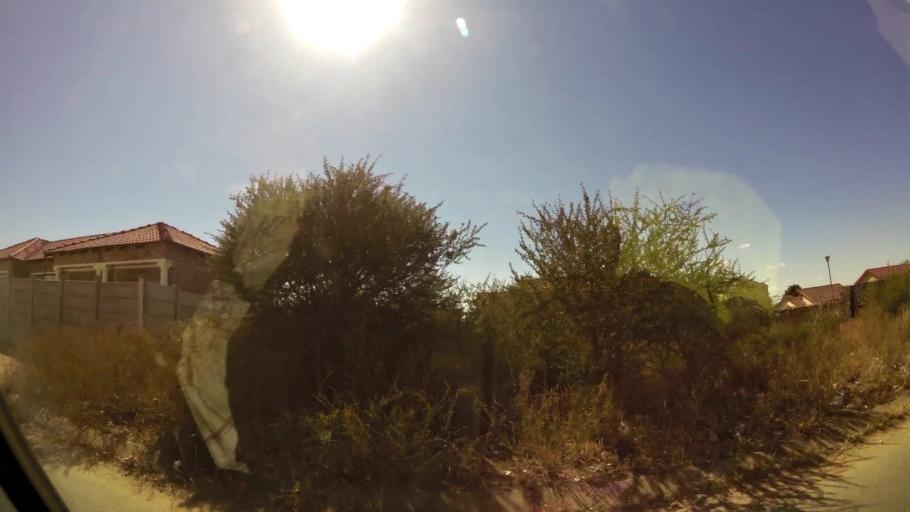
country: ZA
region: Limpopo
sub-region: Capricorn District Municipality
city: Polokwane
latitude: -23.8702
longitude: 29.4272
